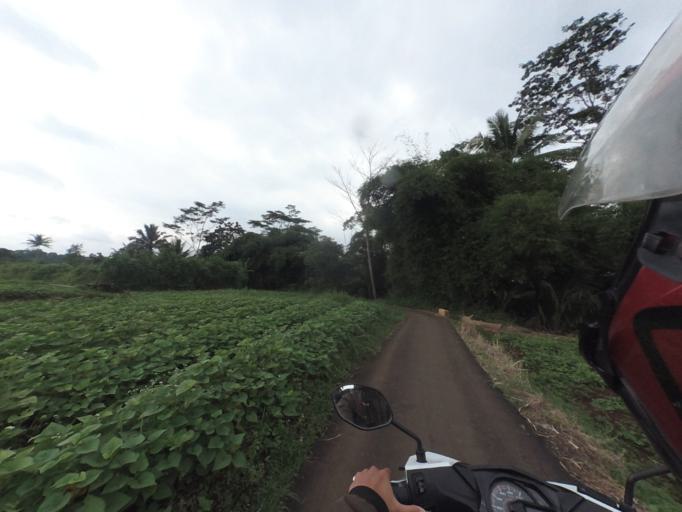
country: ID
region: West Java
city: Ciampea
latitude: -6.5991
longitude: 106.7215
